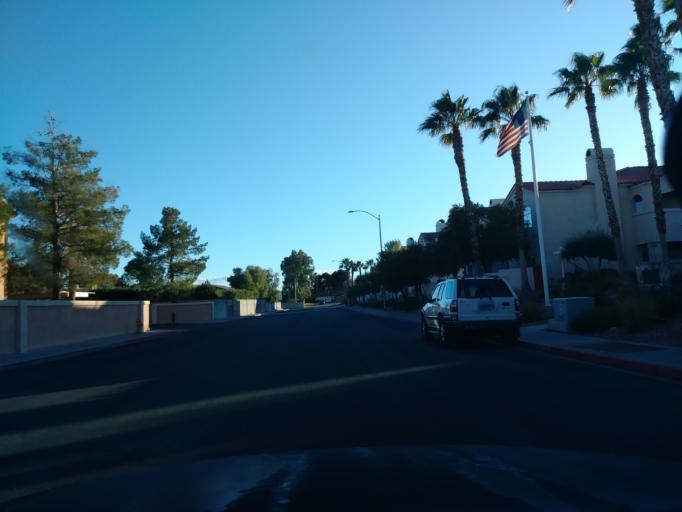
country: US
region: Nevada
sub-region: Clark County
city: Spring Valley
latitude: 36.1531
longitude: -115.2412
